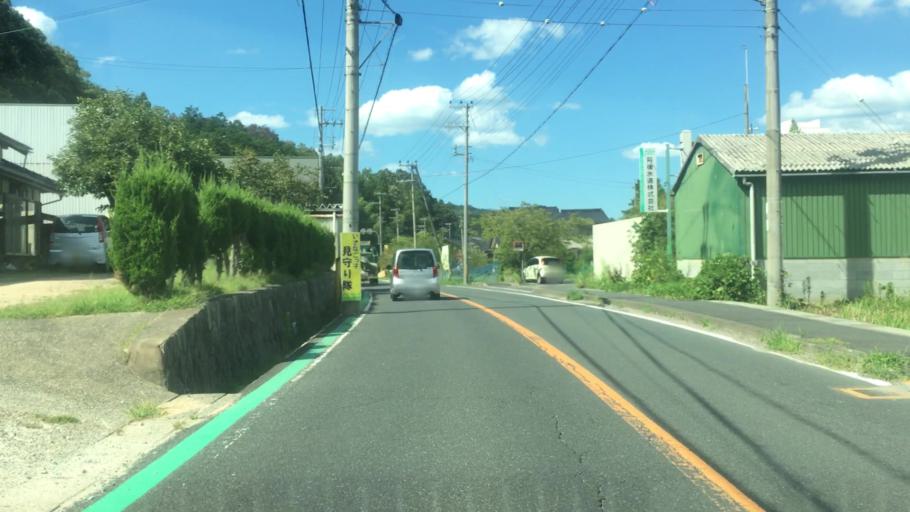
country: JP
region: Kyoto
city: Miyazu
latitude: 35.6157
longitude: 135.0538
